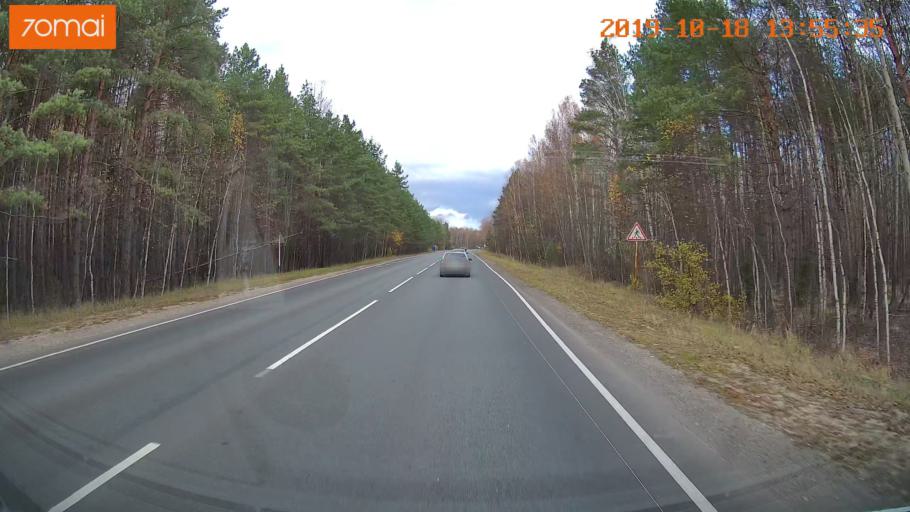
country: RU
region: Rjazan
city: Spas-Klepiki
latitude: 55.0539
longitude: 40.0240
